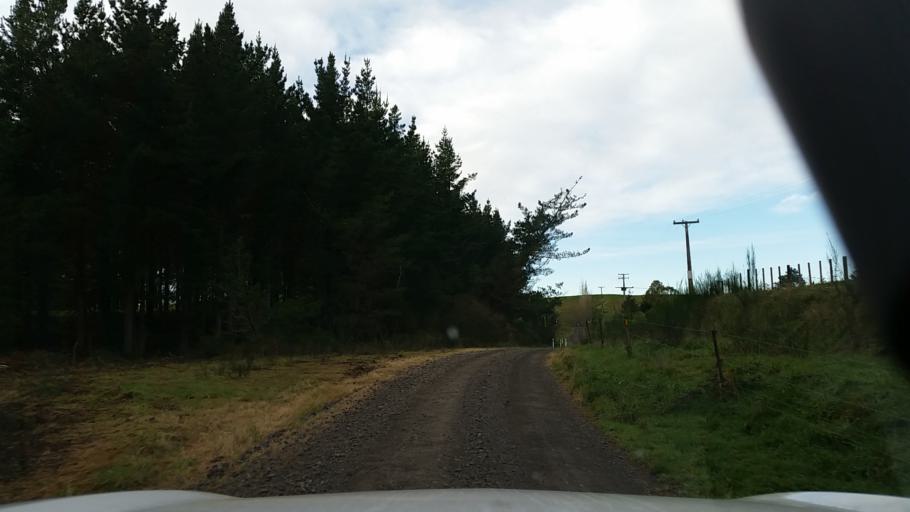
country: NZ
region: Bay of Plenty
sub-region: Rotorua District
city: Rotorua
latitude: -38.2699
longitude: 176.1560
